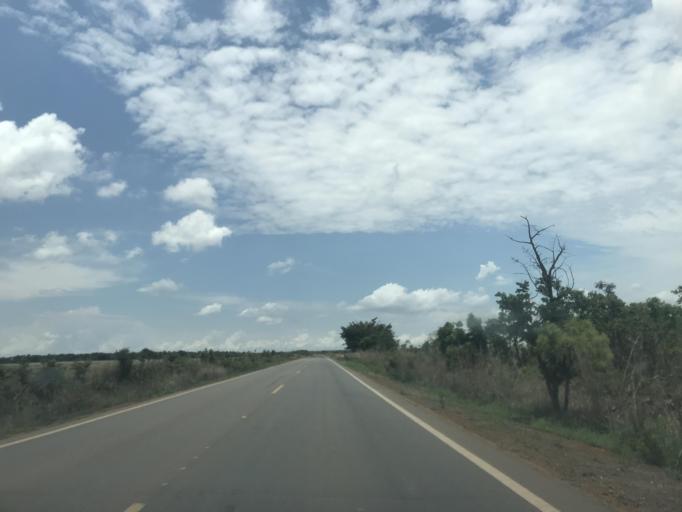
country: BR
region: Goias
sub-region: Luziania
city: Luziania
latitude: -16.5070
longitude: -48.2243
